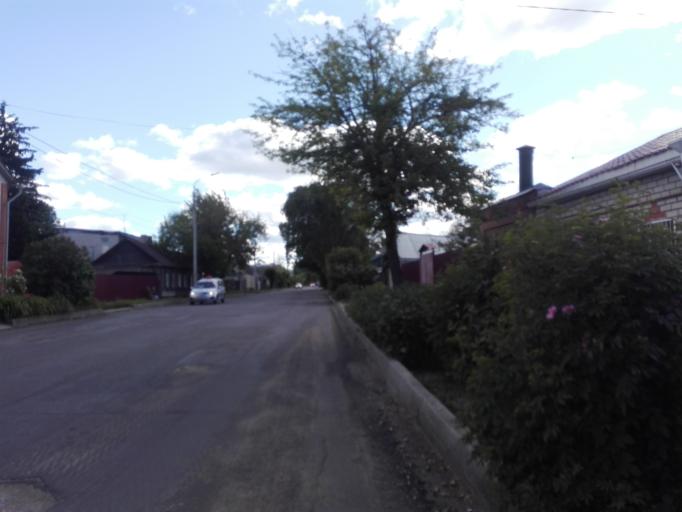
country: RU
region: Orjol
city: Orel
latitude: 52.9565
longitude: 36.0529
